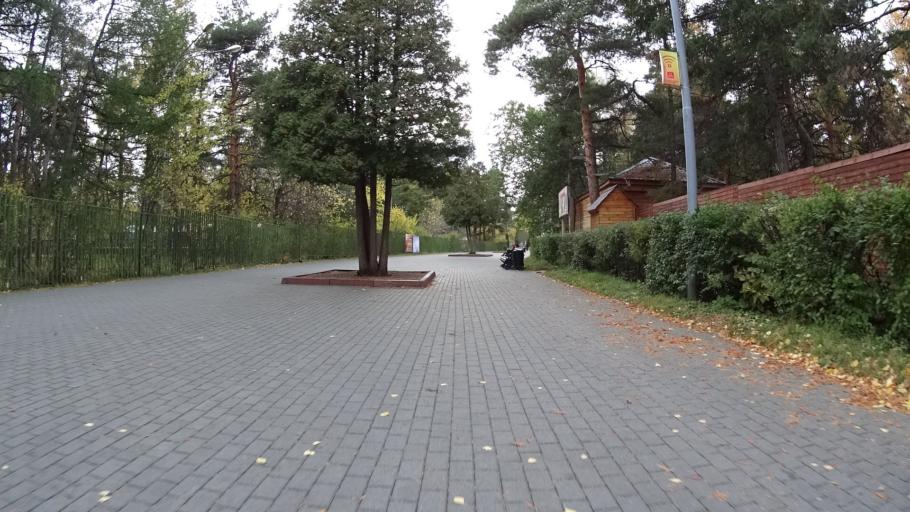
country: RU
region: Chelyabinsk
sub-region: Gorod Chelyabinsk
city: Chelyabinsk
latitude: 55.1647
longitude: 61.3682
